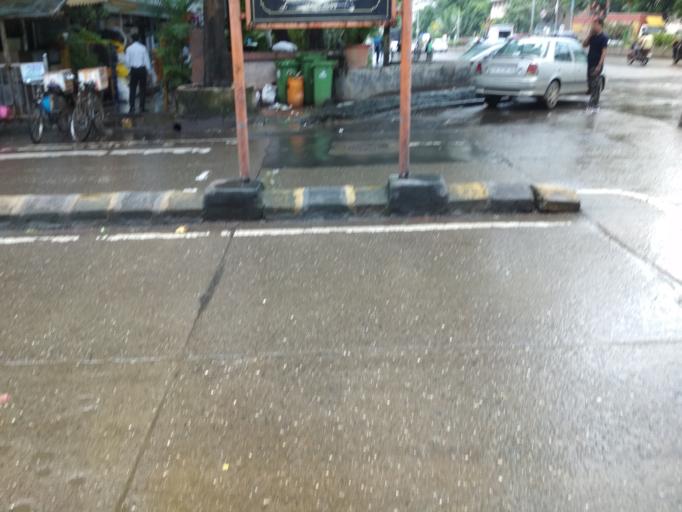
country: IN
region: Maharashtra
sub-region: Thane
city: Thane
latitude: 19.1630
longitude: 72.9416
